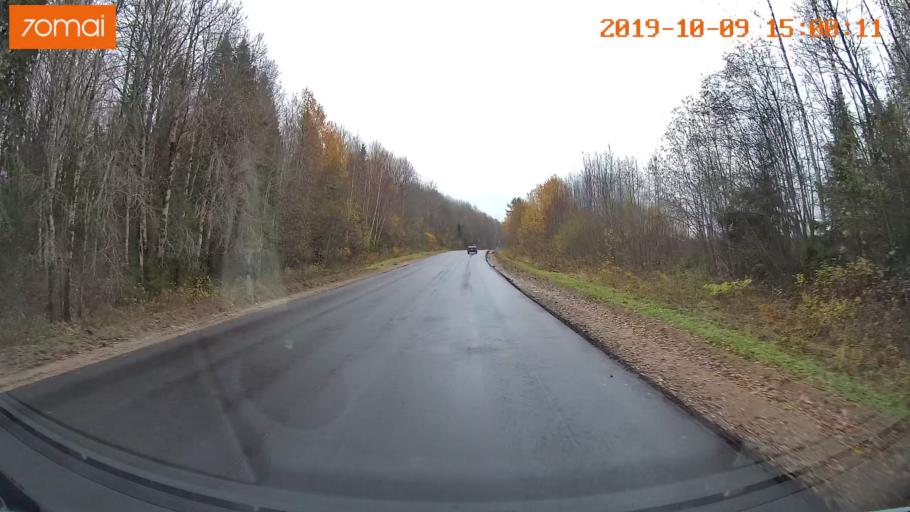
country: RU
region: Kostroma
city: Chistyye Bory
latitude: 58.3121
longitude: 41.6762
